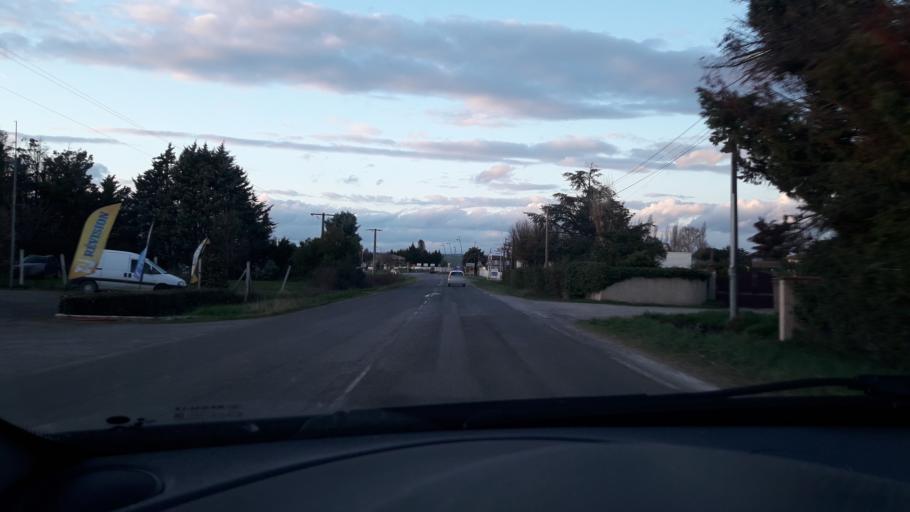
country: FR
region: Midi-Pyrenees
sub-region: Departement du Gers
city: Pujaudran
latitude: 43.6088
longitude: 1.0998
